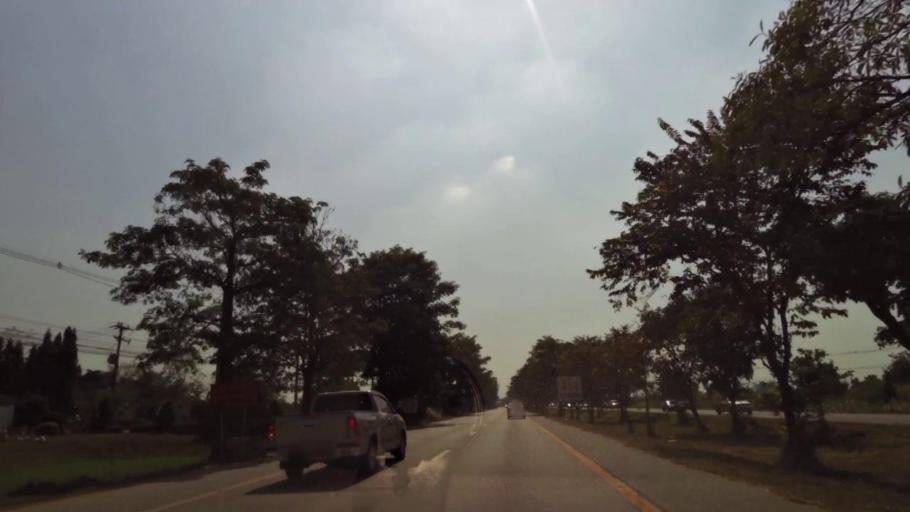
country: TH
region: Phichit
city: Wachira Barami
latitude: 16.5176
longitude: 100.1429
